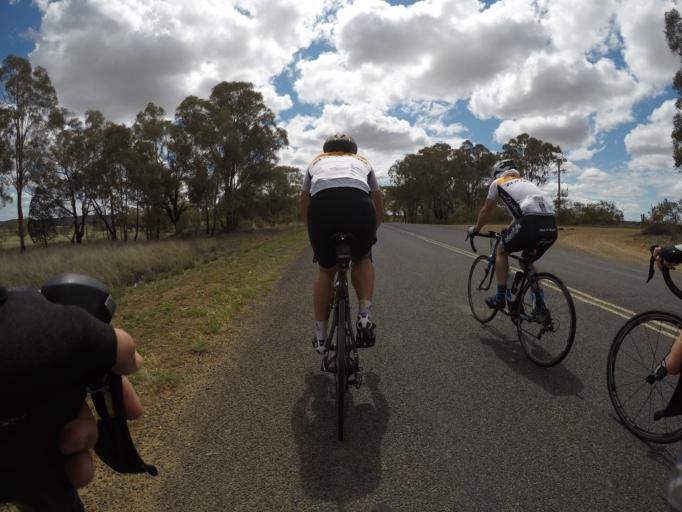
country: AU
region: New South Wales
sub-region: Dubbo Municipality
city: Dubbo
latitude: -32.4735
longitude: 148.5650
